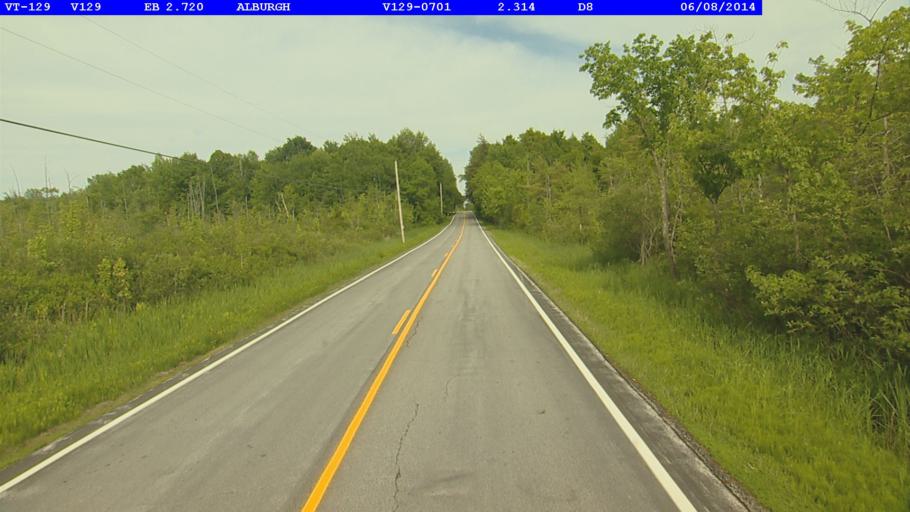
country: US
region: Vermont
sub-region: Grand Isle County
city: North Hero
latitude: 44.8874
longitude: -73.2875
